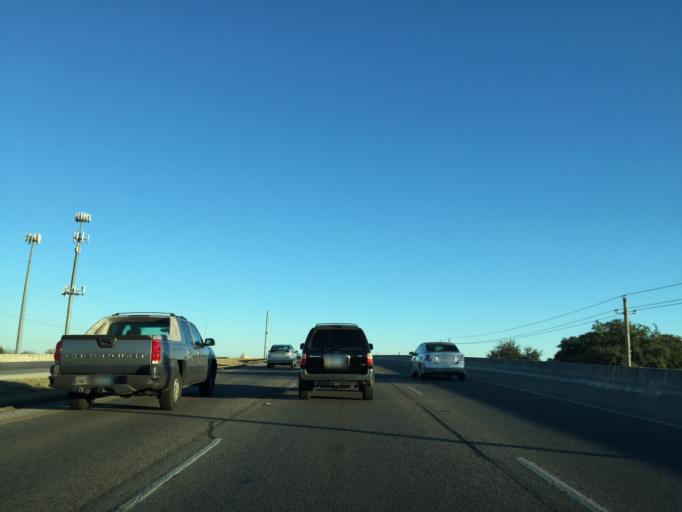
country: US
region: Texas
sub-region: Williamson County
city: Jollyville
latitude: 30.4336
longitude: -97.7310
